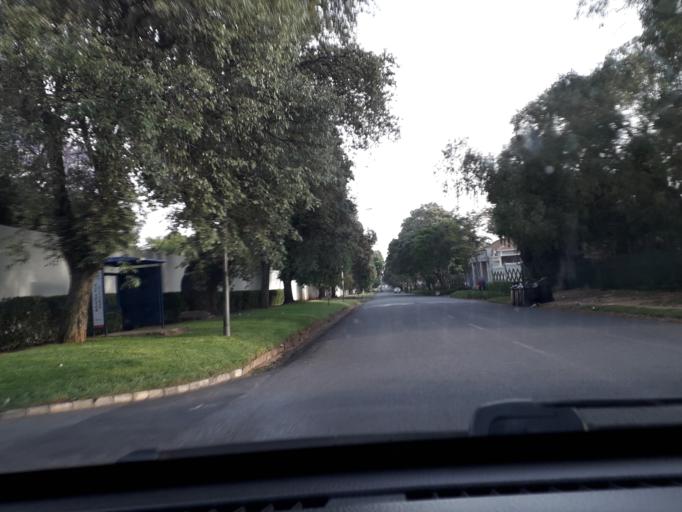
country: ZA
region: Gauteng
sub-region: City of Johannesburg Metropolitan Municipality
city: Johannesburg
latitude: -26.1651
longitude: 28.0651
